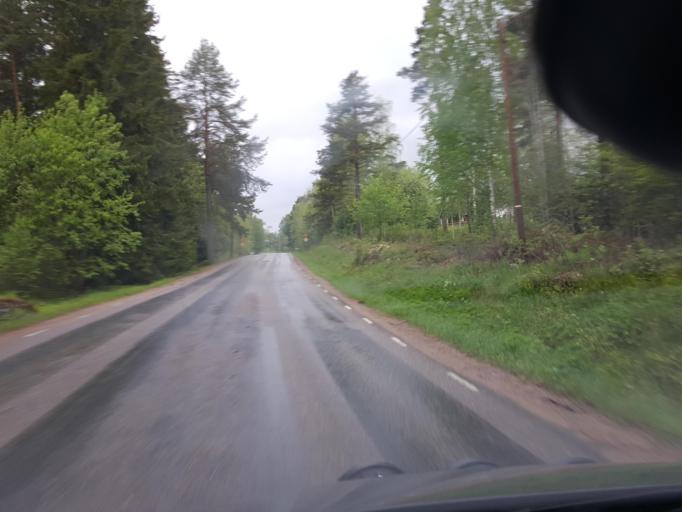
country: SE
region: Gaevleborg
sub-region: Ljusdals Kommun
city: Ljusdal
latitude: 61.8173
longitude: 16.1402
